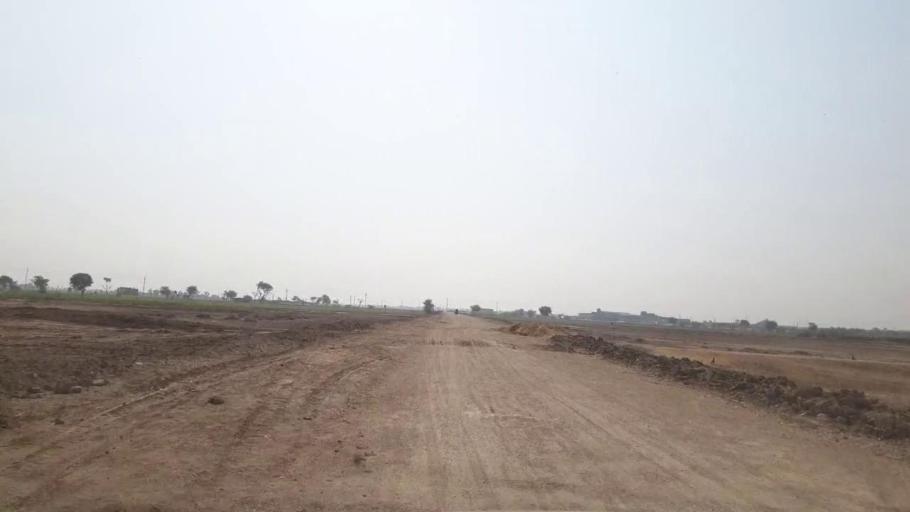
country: PK
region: Sindh
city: Mirpur Khas
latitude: 25.5564
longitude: 69.0477
